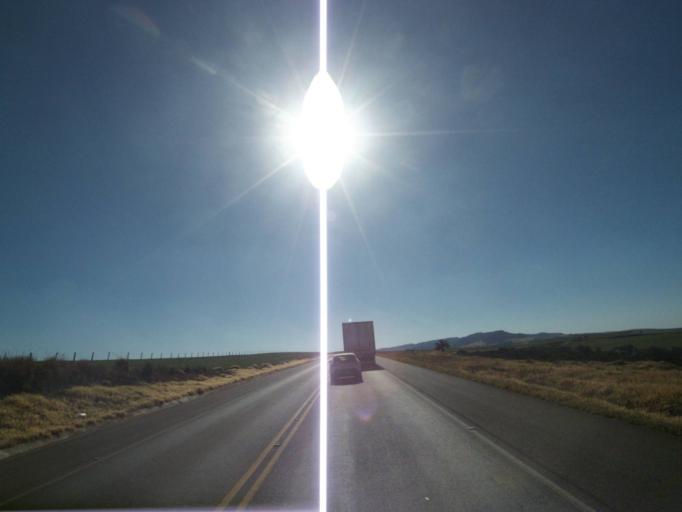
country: BR
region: Parana
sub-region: Tibagi
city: Tibagi
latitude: -24.6398
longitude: -50.4581
